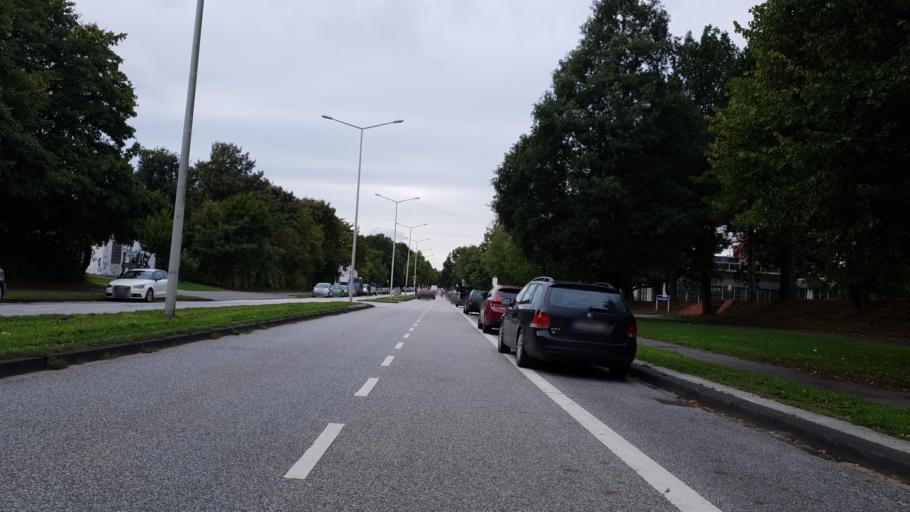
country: DE
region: Schleswig-Holstein
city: Kiel
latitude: 54.3420
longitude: 10.1135
